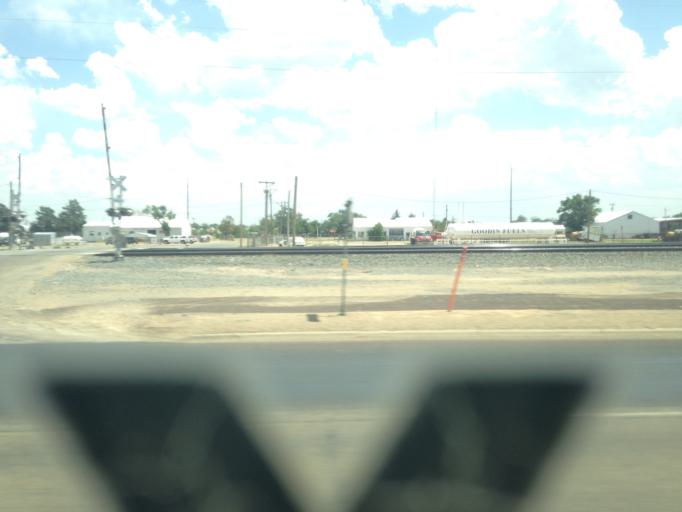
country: US
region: Texas
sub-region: Deaf Smith County
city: Hereford
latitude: 34.8220
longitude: -102.3839
